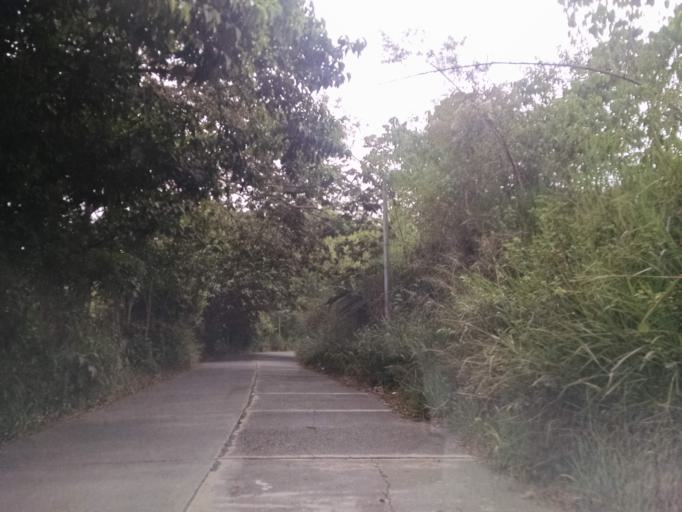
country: CO
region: Valle del Cauca
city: Alcala
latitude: 4.6906
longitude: -75.7761
